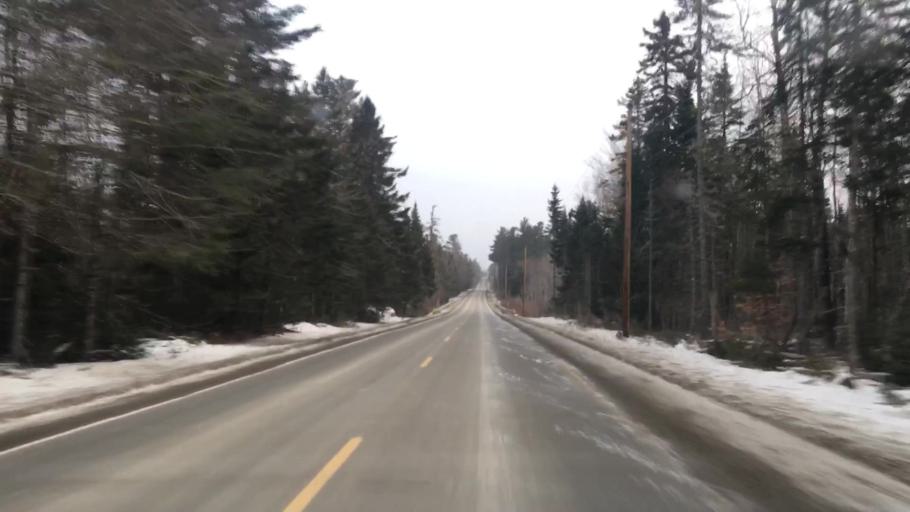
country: US
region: Maine
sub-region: Hancock County
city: Ellsworth
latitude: 44.6705
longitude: -68.3545
